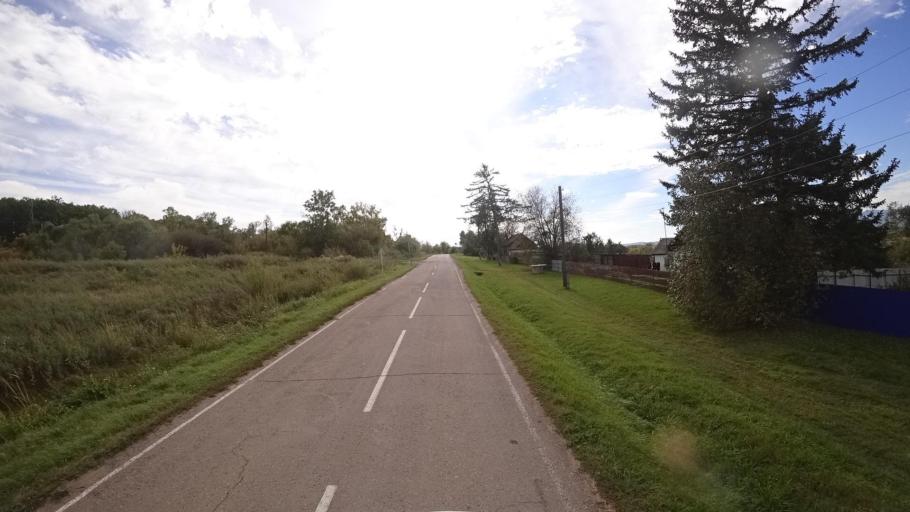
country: RU
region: Primorskiy
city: Dostoyevka
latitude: 44.3295
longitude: 133.4796
